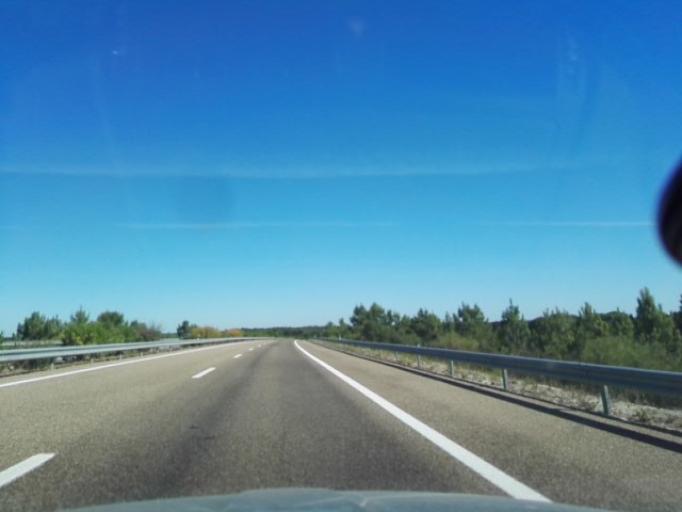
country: PT
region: Evora
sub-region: Vendas Novas
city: Vendas Novas
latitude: 38.6468
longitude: -8.6658
